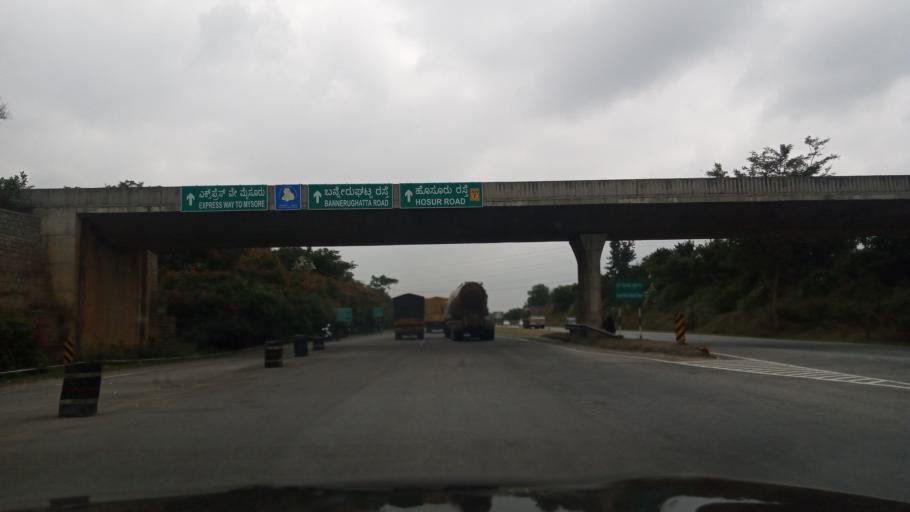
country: IN
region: Karnataka
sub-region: Bangalore Rural
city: Nelamangala
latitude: 13.0407
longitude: 77.4756
